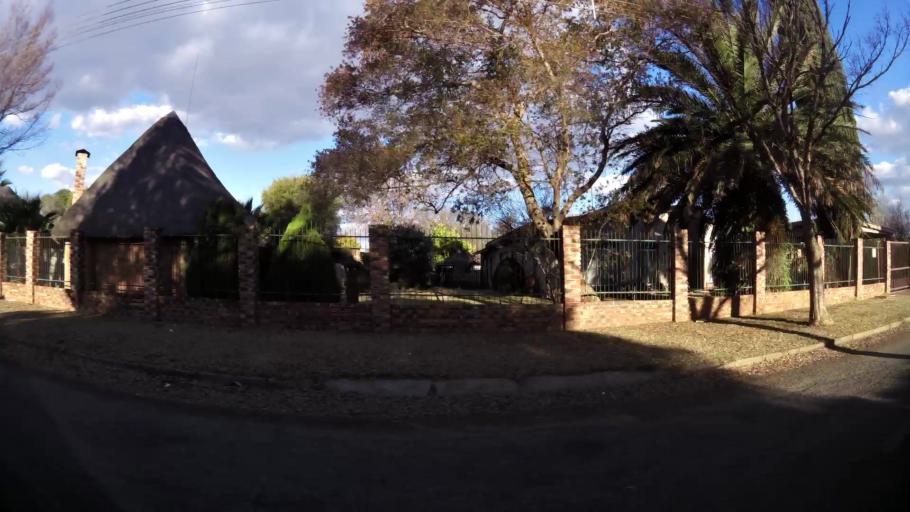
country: ZA
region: North-West
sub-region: Dr Kenneth Kaunda District Municipality
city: Potchefstroom
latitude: -26.7421
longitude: 27.0891
